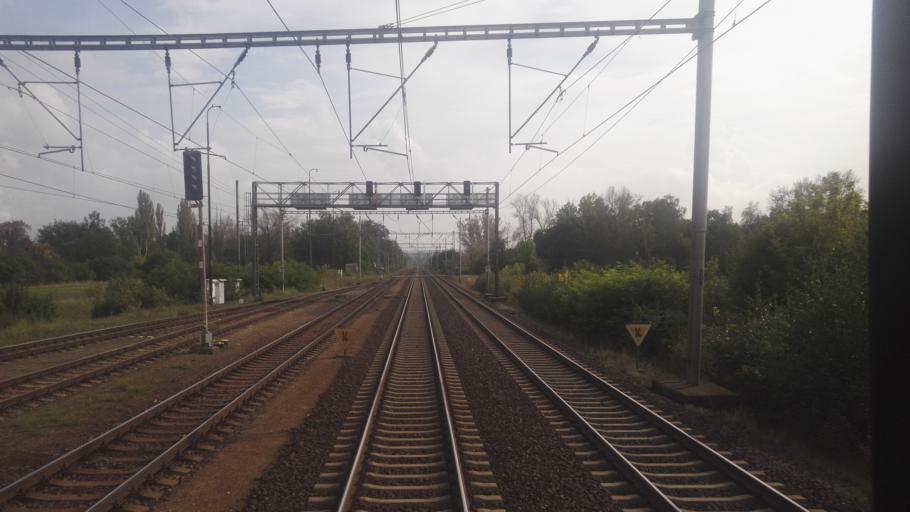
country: CZ
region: Ustecky
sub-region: Okres Litomerice
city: Steti
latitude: 50.4400
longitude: 14.3685
